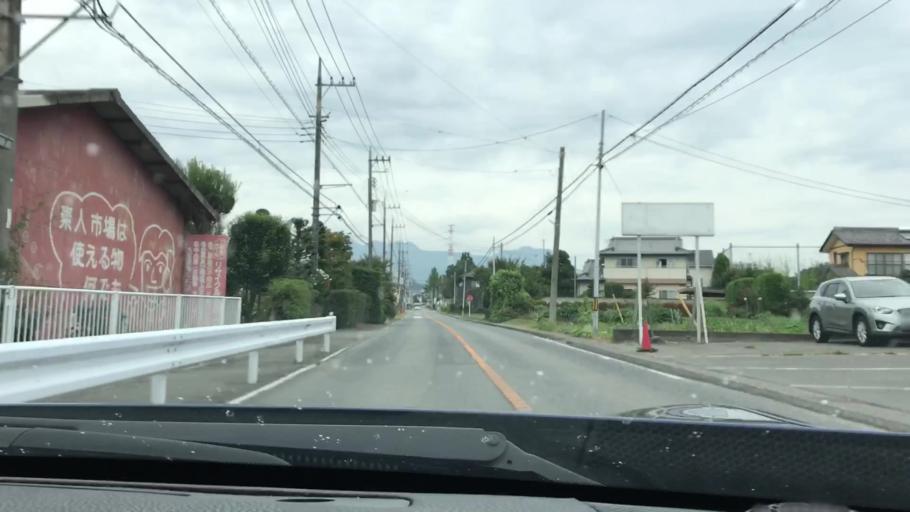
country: JP
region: Gunma
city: Kanekomachi
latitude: 36.3847
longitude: 138.9850
